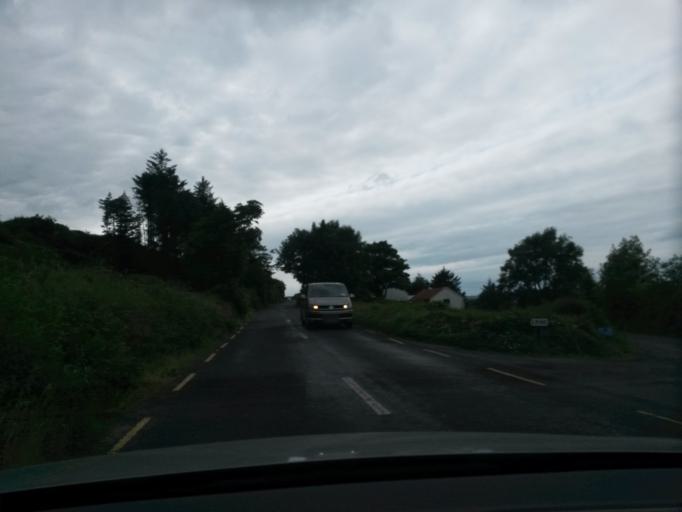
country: IE
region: Connaught
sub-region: County Galway
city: Bearna
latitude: 52.9795
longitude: -9.2494
